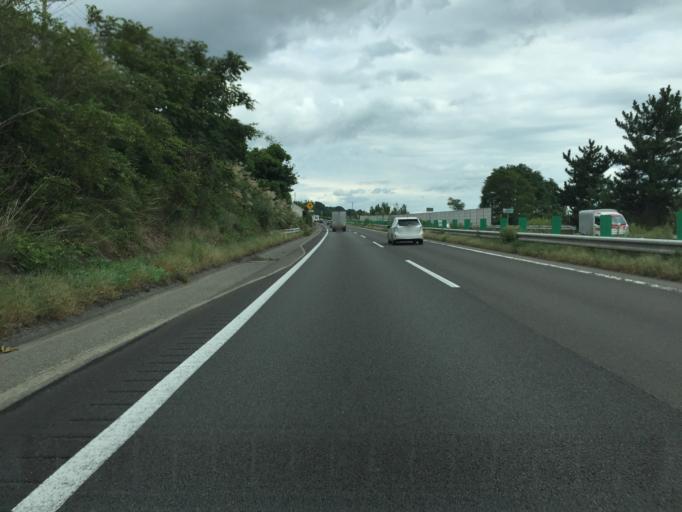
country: JP
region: Fukushima
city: Hobaramachi
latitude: 37.8291
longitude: 140.4853
